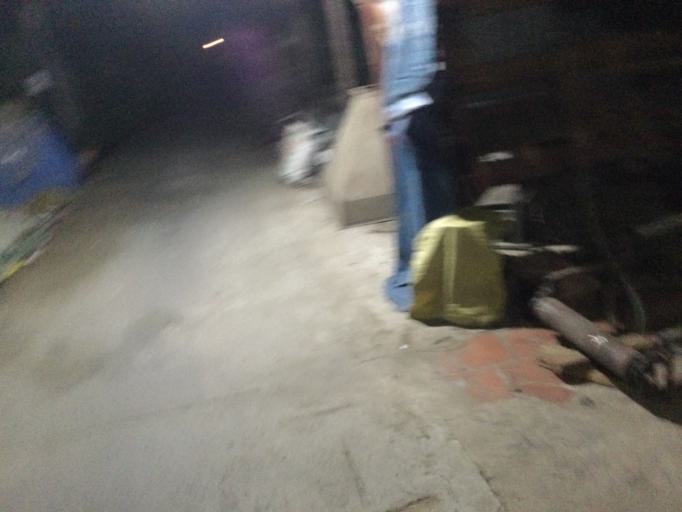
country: VN
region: Kien Giang
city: Tan Hiep
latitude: 10.1204
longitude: 105.2827
